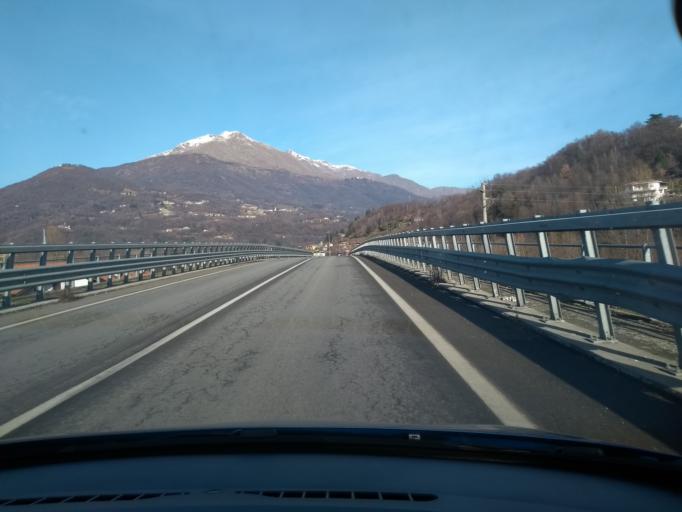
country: IT
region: Piedmont
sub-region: Provincia di Torino
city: Cuorgne
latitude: 45.3920
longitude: 7.6603
